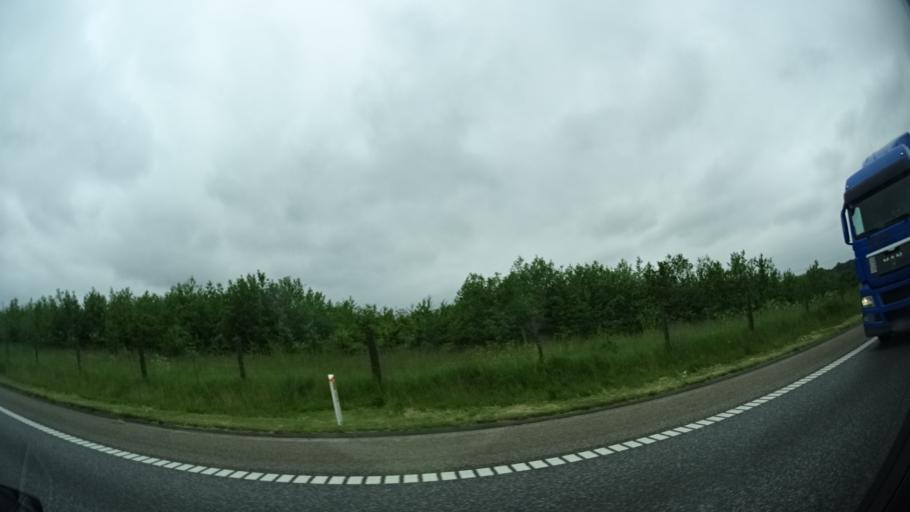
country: DK
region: Central Jutland
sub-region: Arhus Kommune
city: Sabro
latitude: 56.1842
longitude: 10.0698
